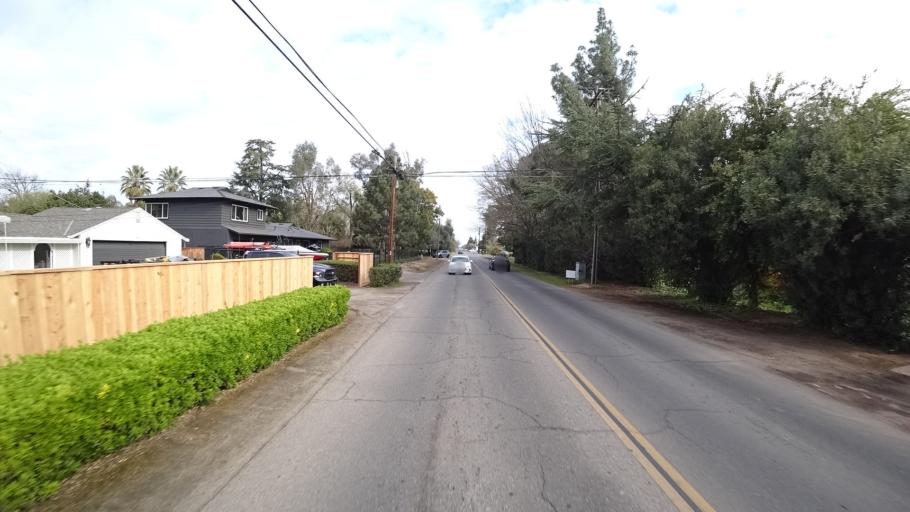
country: US
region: California
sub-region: Fresno County
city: Fresno
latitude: 36.8060
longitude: -119.7995
